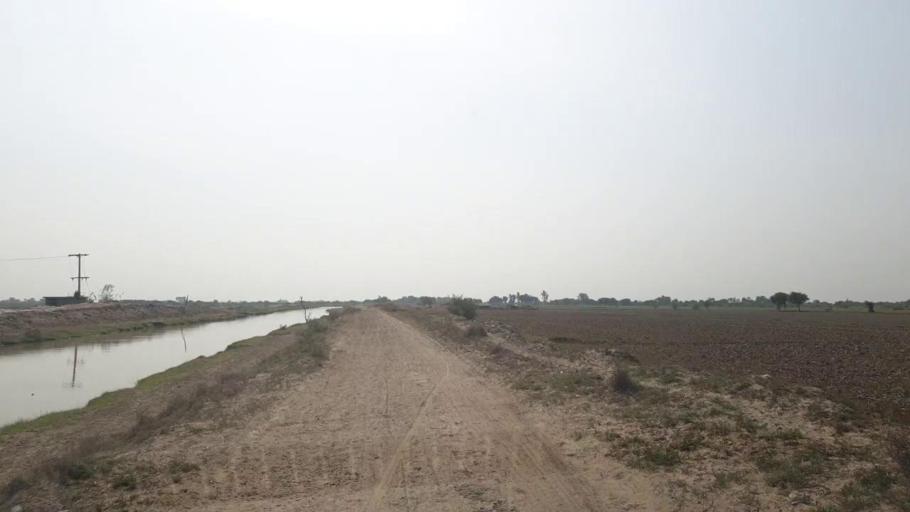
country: PK
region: Sindh
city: Badin
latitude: 24.5498
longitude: 68.8499
